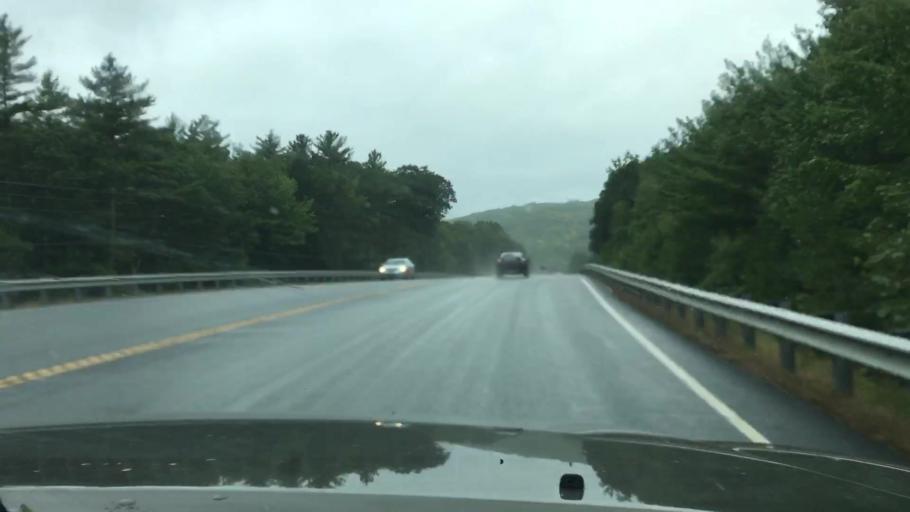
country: US
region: New Hampshire
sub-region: Cheshire County
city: Keene
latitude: 42.9677
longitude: -72.2495
